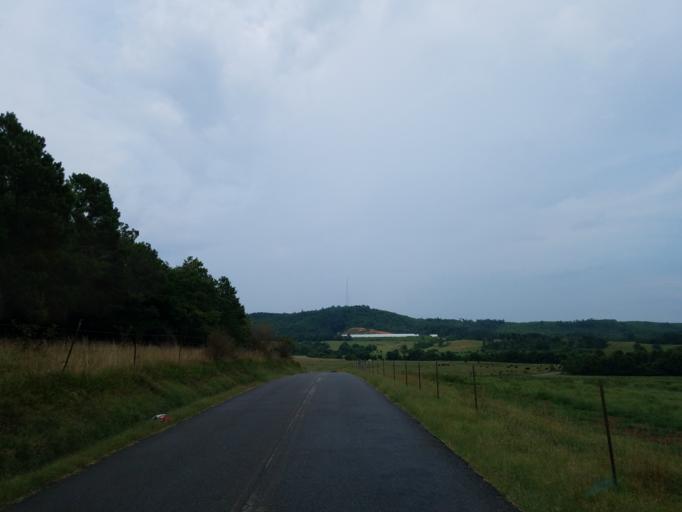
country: US
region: Georgia
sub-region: Bartow County
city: Rydal
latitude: 34.3726
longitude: -84.7064
